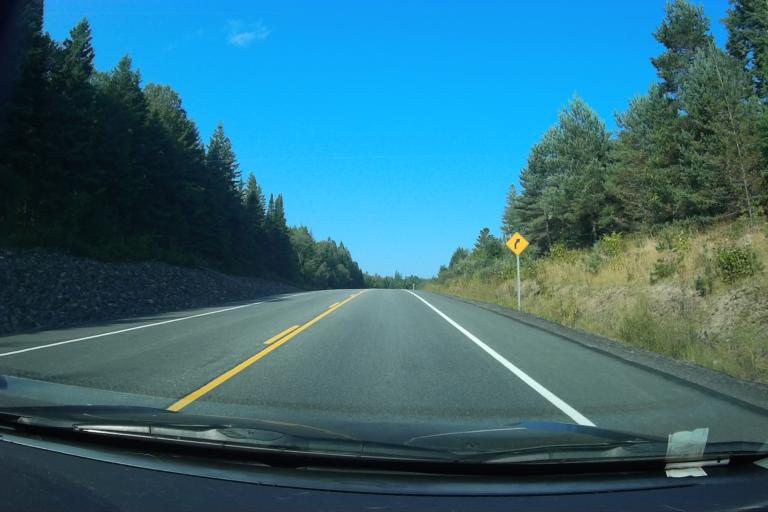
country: CA
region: Ontario
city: Huntsville
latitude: 45.5527
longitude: -78.6102
